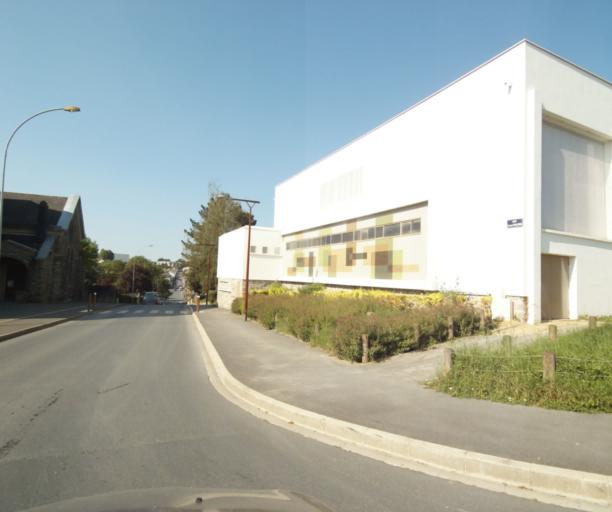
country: FR
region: Champagne-Ardenne
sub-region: Departement des Ardennes
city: Charleville-Mezieres
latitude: 49.7819
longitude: 4.7117
